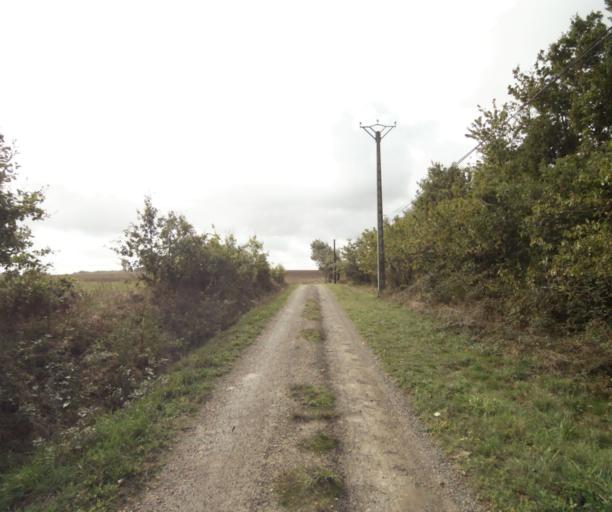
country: FR
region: Midi-Pyrenees
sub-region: Departement du Tarn-et-Garonne
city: Beaumont-de-Lomagne
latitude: 43.8822
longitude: 1.0753
